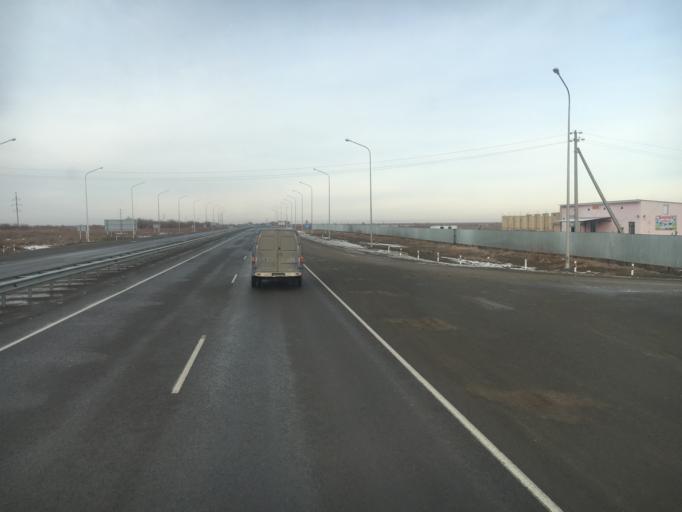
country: KZ
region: Qyzylorda
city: Shieli
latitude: 44.1400
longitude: 66.9647
